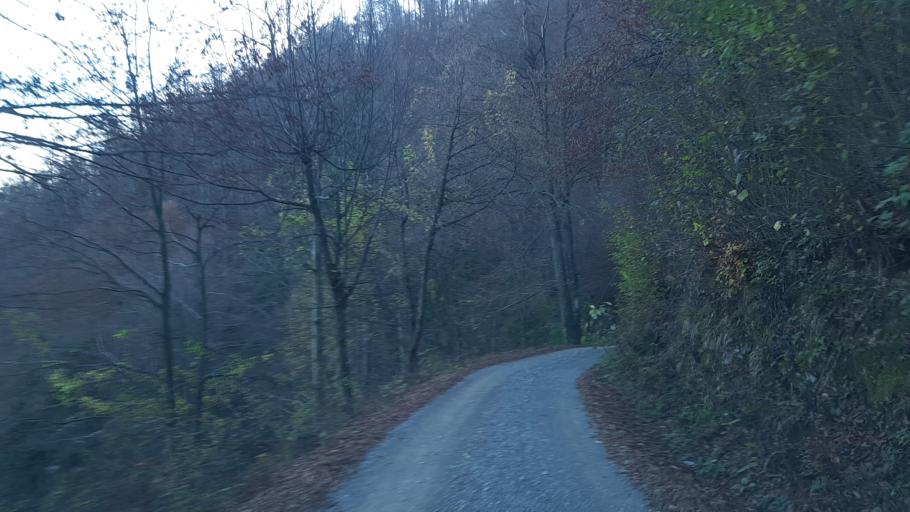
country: SI
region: Borovnica
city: Borovnica
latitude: 45.9272
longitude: 14.3417
